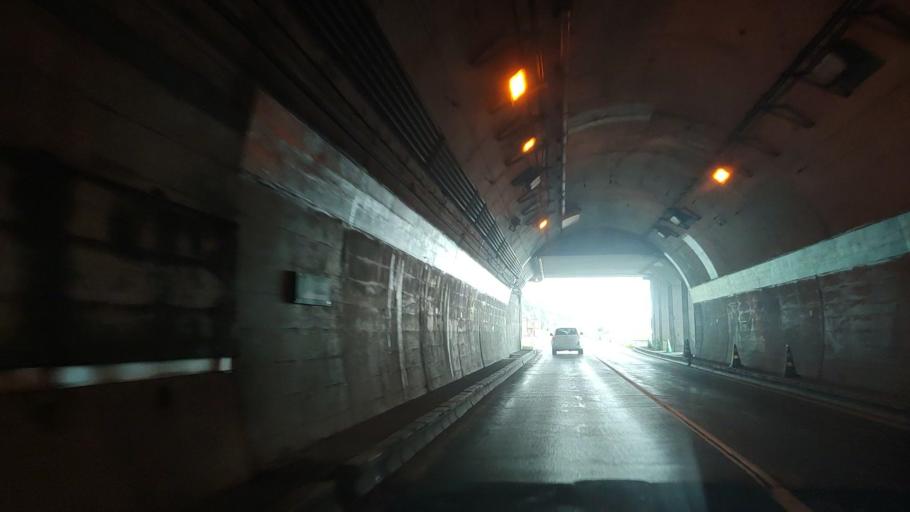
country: JP
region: Hokkaido
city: Rumoi
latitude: 43.7899
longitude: 141.3723
